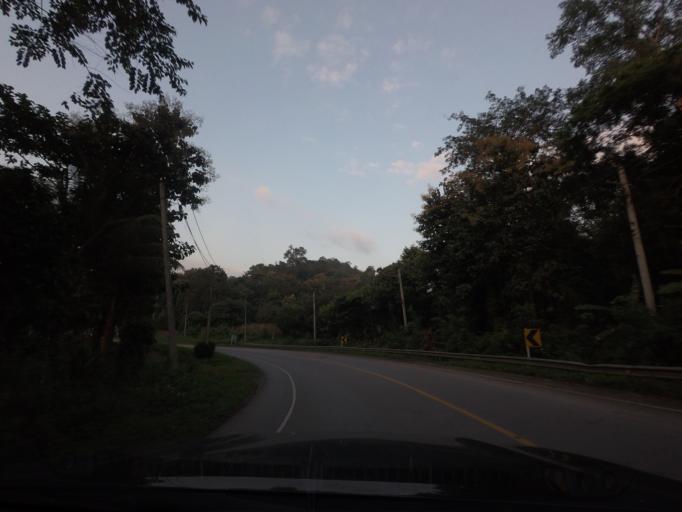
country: TH
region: Nan
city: Na Noi
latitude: 18.4107
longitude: 100.7020
